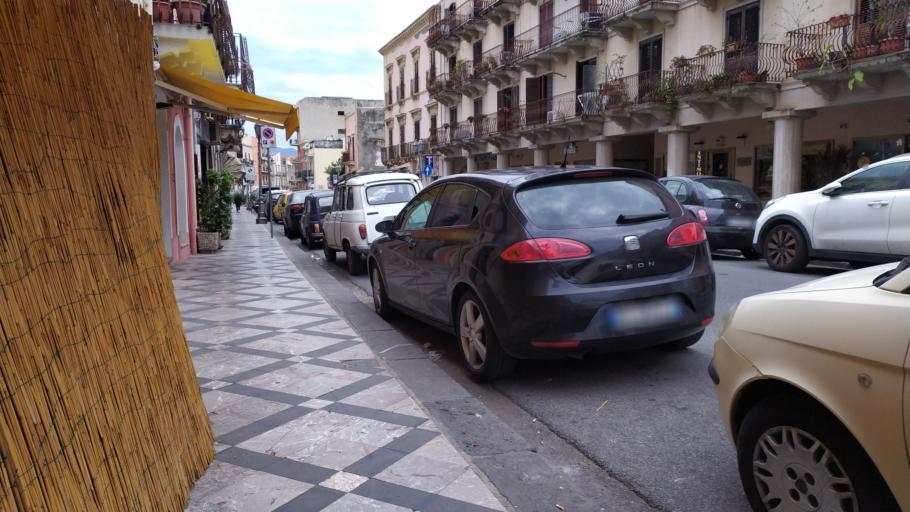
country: IT
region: Sicily
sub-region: Messina
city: Milazzo
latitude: 38.2223
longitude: 15.2408
